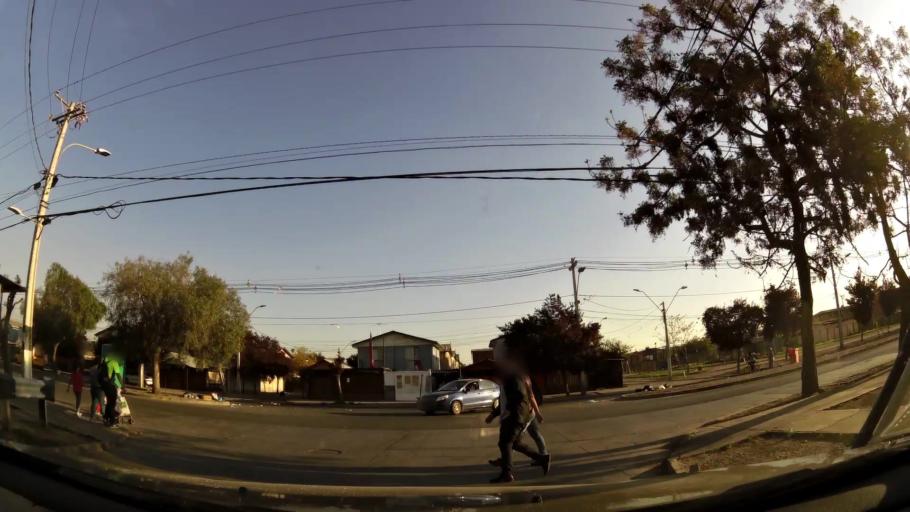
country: CL
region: Santiago Metropolitan
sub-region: Provincia de Maipo
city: San Bernardo
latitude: -33.5952
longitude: -70.6724
